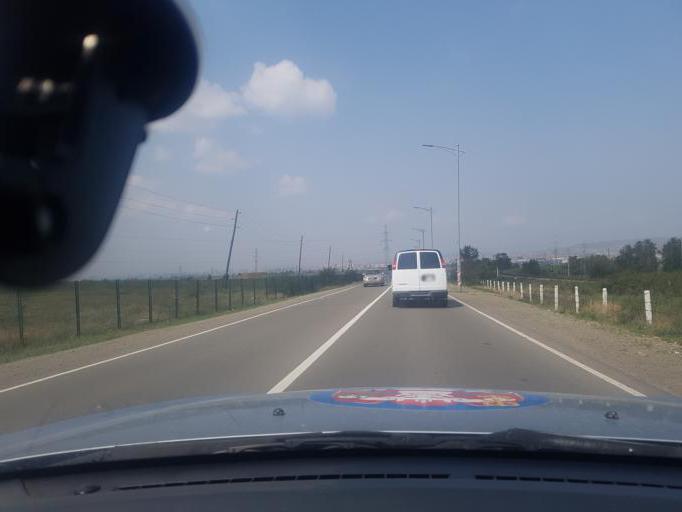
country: MN
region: Ulaanbaatar
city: Ulaanbaatar
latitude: 47.8899
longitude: 107.0429
